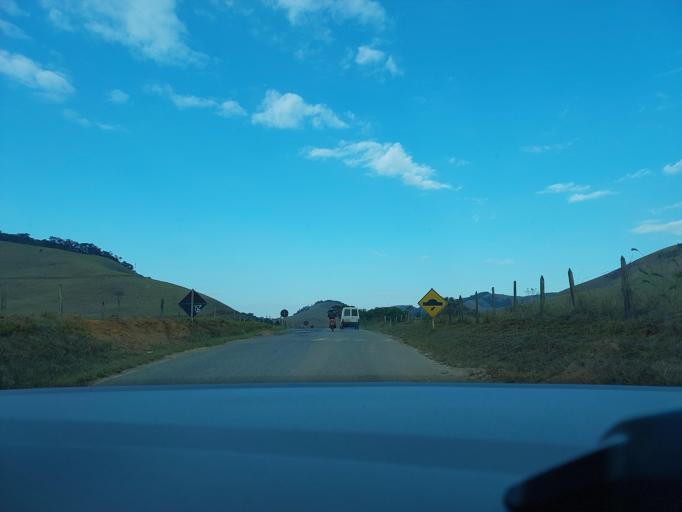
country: BR
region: Minas Gerais
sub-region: Muriae
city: Muriae
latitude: -21.0499
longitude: -42.5184
